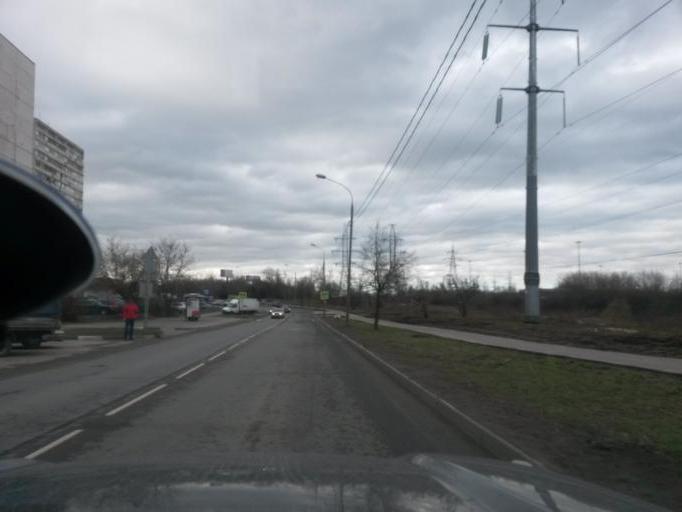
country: RU
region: Moskovskaya
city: Biryulevo Zapadnoye
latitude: 55.5767
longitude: 37.6436
